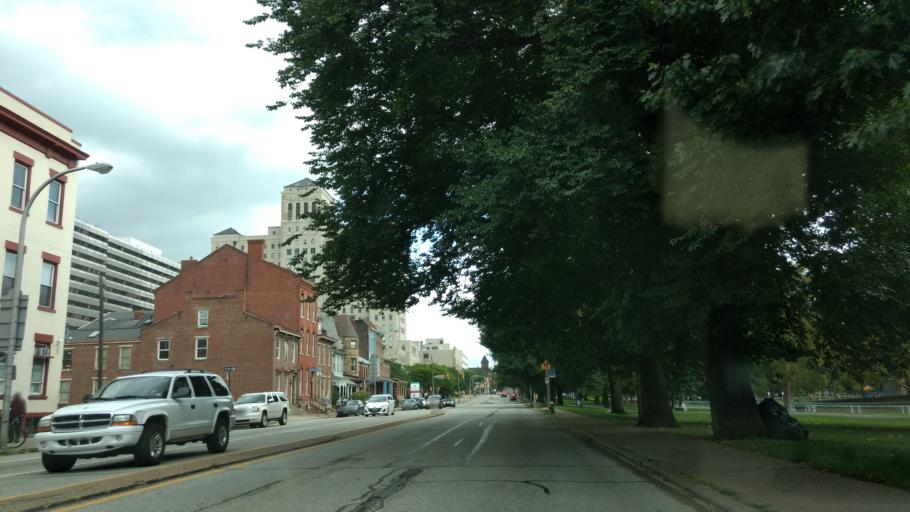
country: US
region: Pennsylvania
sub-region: Allegheny County
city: Pittsburgh
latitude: 40.4554
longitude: -80.0064
